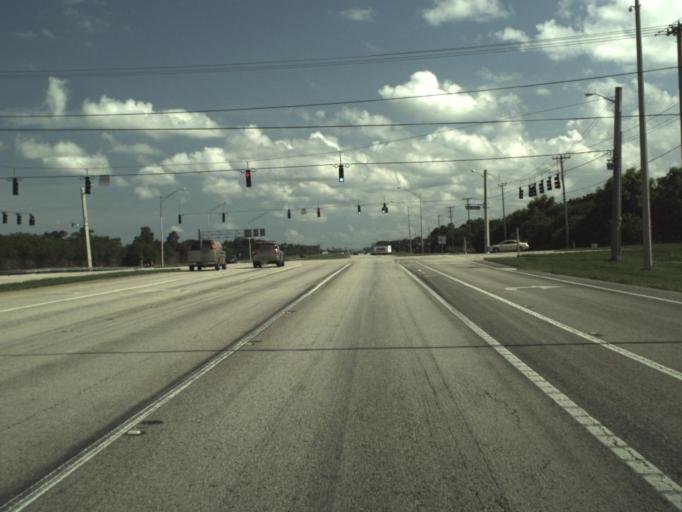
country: US
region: Florida
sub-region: Palm Beach County
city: Villages of Oriole
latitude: 26.4548
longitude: -80.2047
